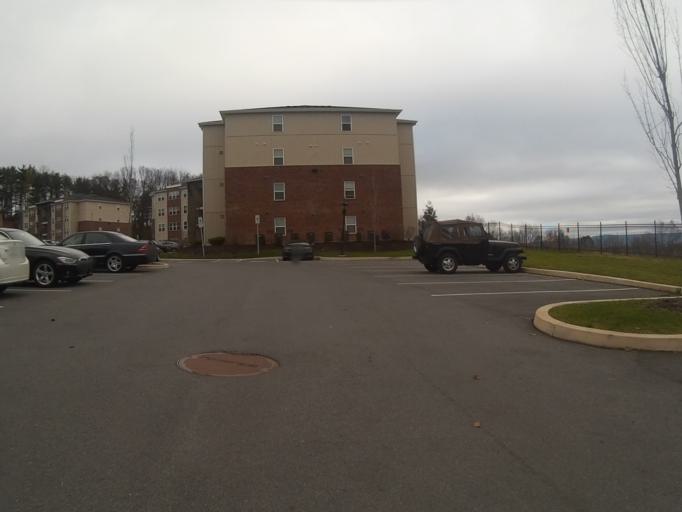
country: US
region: Pennsylvania
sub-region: Centre County
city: Park Forest Village
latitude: 40.8222
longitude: -77.8843
